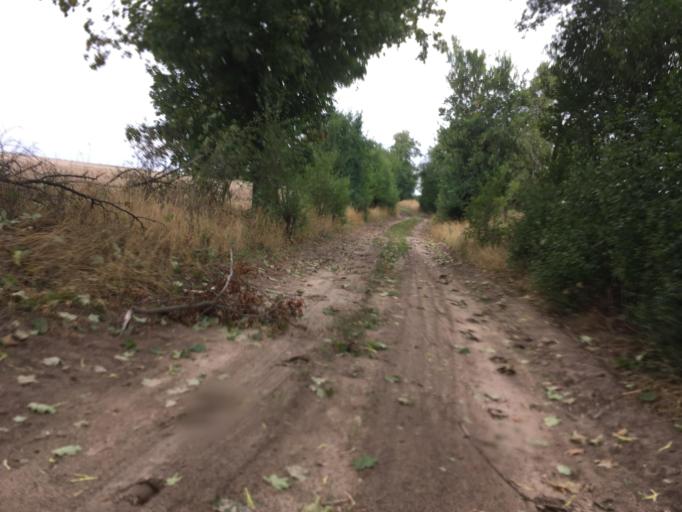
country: DE
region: Brandenburg
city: Passow
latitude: 53.1282
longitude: 14.1057
